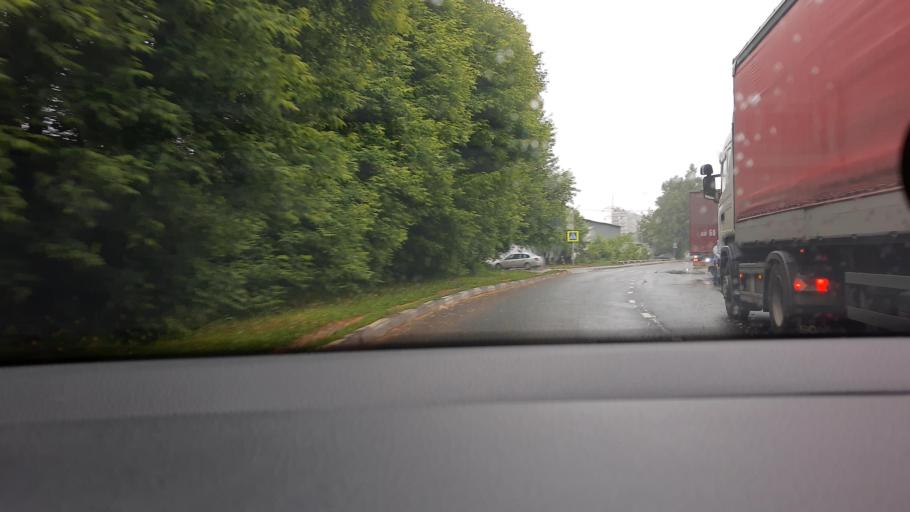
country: RU
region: Moskovskaya
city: Lyubertsy
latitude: 55.6651
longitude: 37.8919
